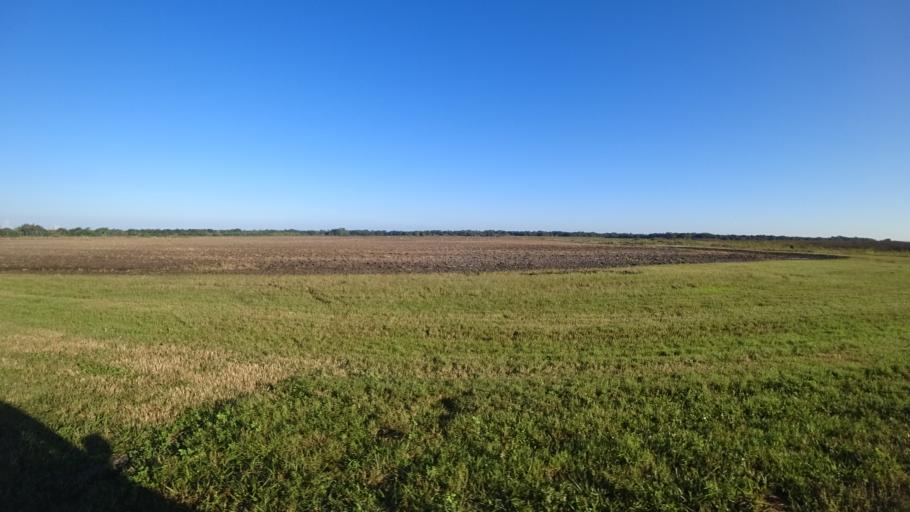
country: US
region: Florida
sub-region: Manatee County
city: Memphis
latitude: 27.6308
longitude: -82.5104
